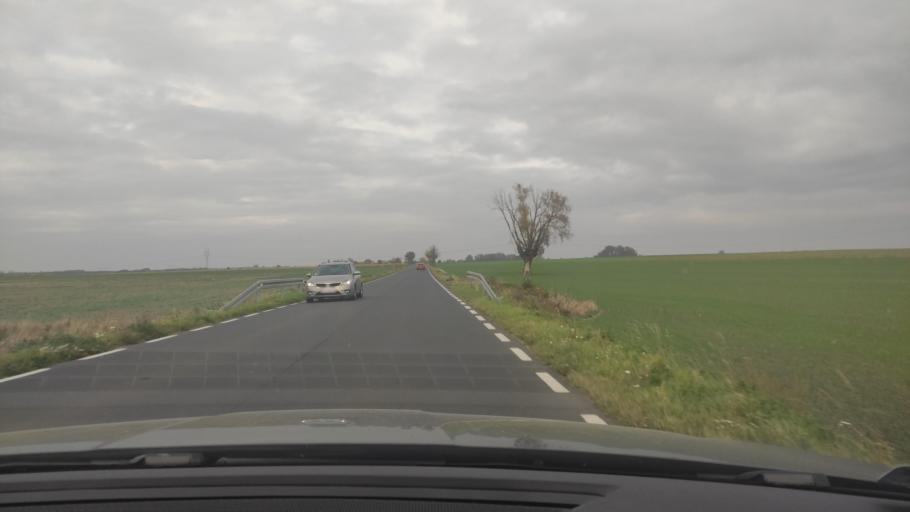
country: PL
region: Greater Poland Voivodeship
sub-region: Powiat poznanski
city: Kostrzyn
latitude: 52.4314
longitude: 17.1594
